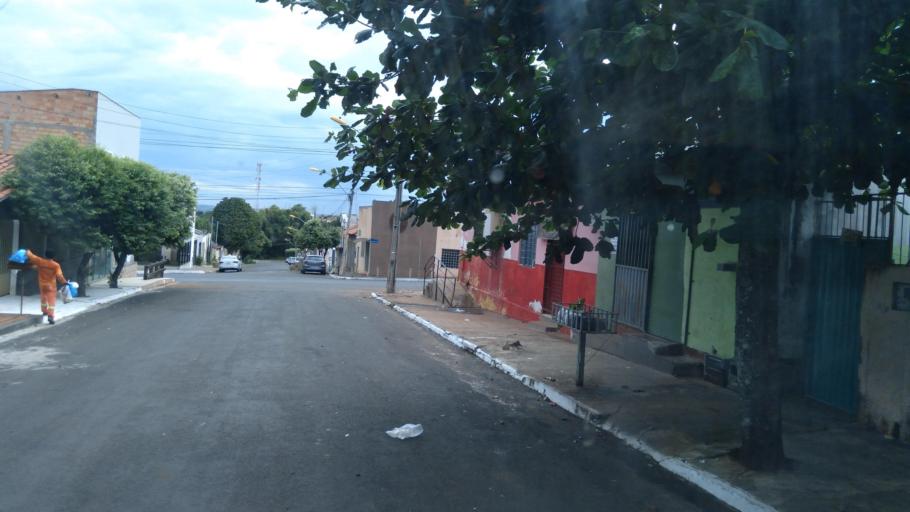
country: BR
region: Goias
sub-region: Mineiros
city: Mineiros
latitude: -17.5680
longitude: -52.5610
